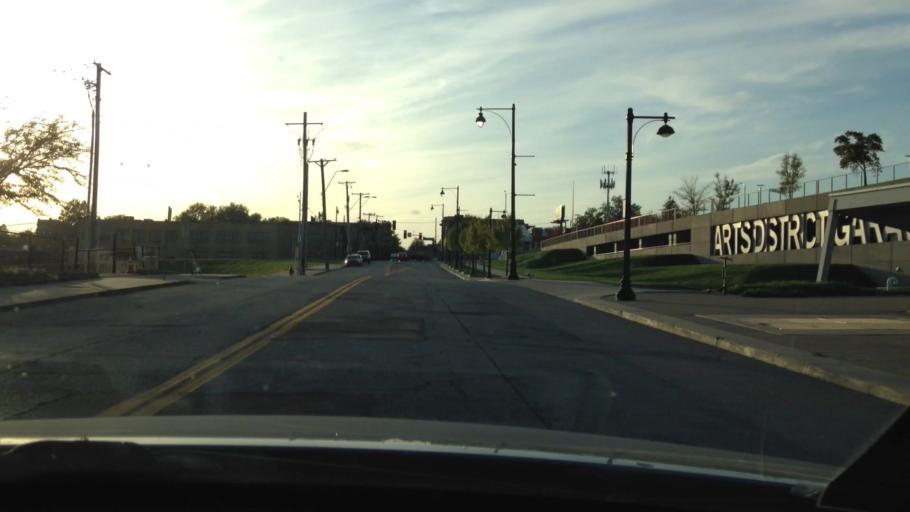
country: US
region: Missouri
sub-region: Jackson County
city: Kansas City
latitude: 39.0928
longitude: -94.5867
